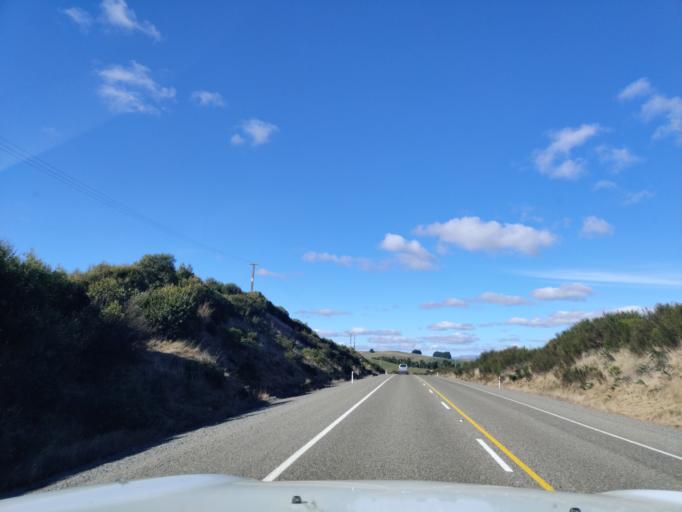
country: NZ
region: Manawatu-Wanganui
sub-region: Ruapehu District
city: Waiouru
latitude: -39.5811
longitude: 175.7267
